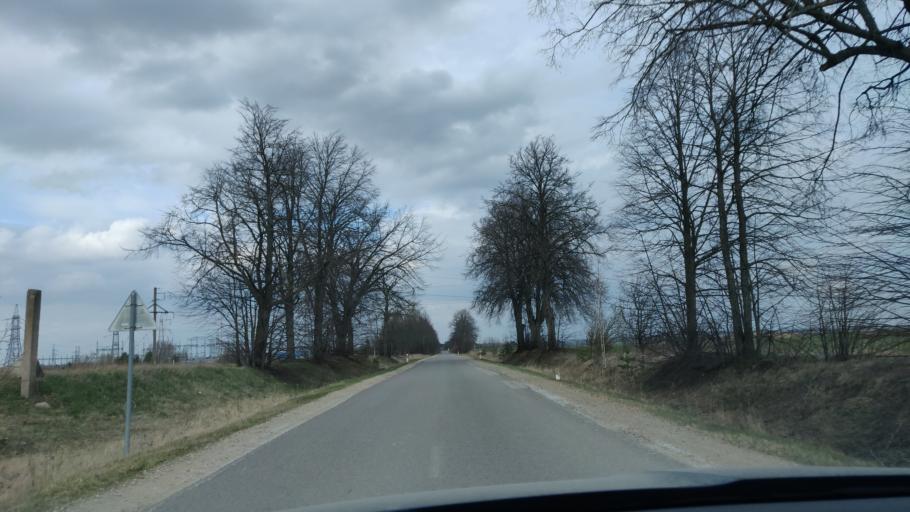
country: LT
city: Lentvaris
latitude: 54.6066
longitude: 25.1106
